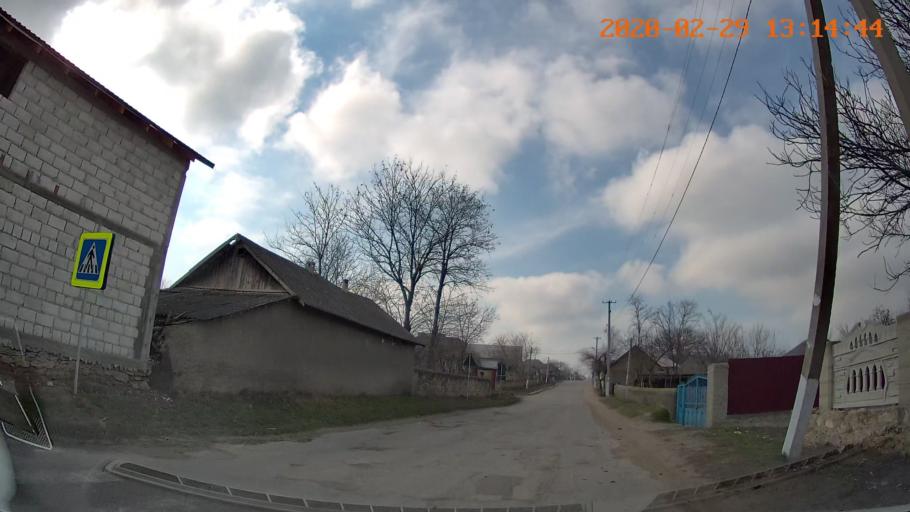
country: MD
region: Telenesti
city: Camenca
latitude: 48.0114
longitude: 28.6756
